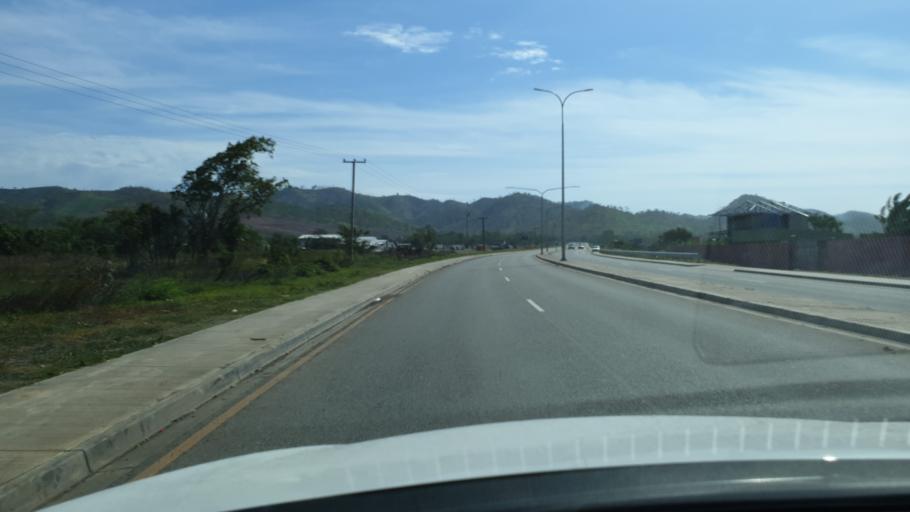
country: PG
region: National Capital
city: Port Moresby
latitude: -9.4779
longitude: 147.2423
